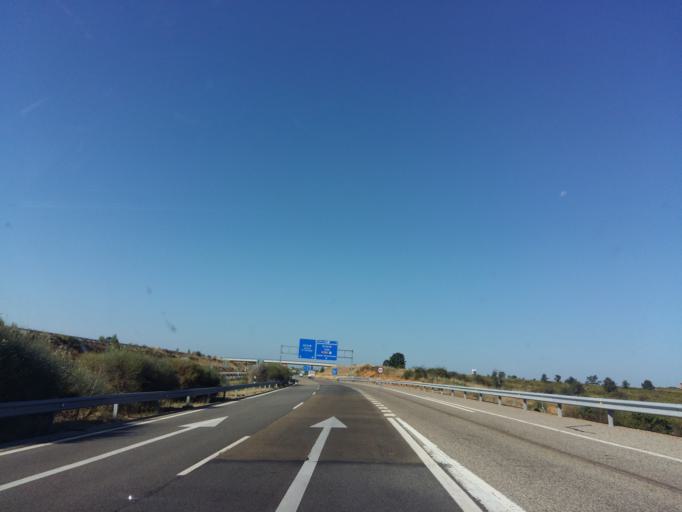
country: ES
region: Castille and Leon
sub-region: Provincia de Leon
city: San Andres del Rabanedo
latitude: 42.5758
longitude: -5.6282
